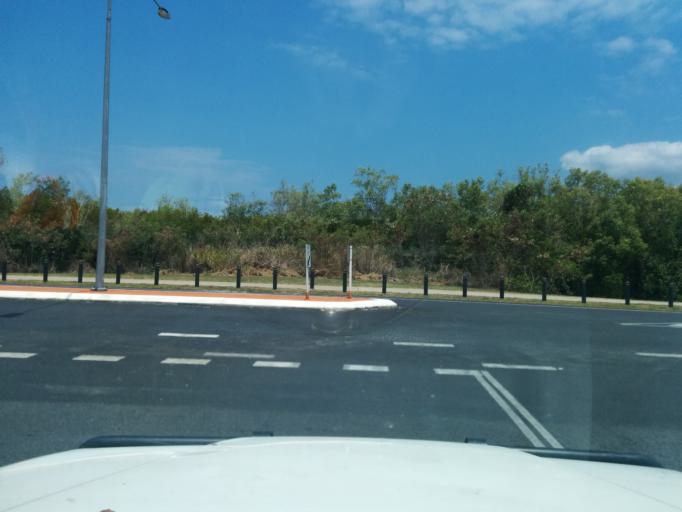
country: AU
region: Queensland
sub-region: Cairns
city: Cairns
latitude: -16.8975
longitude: 145.7576
